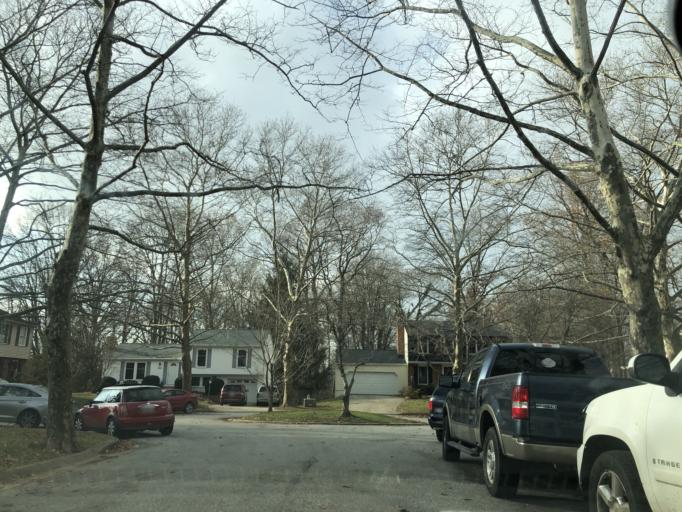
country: US
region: Maryland
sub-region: Howard County
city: Columbia
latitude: 39.1984
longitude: -76.8387
